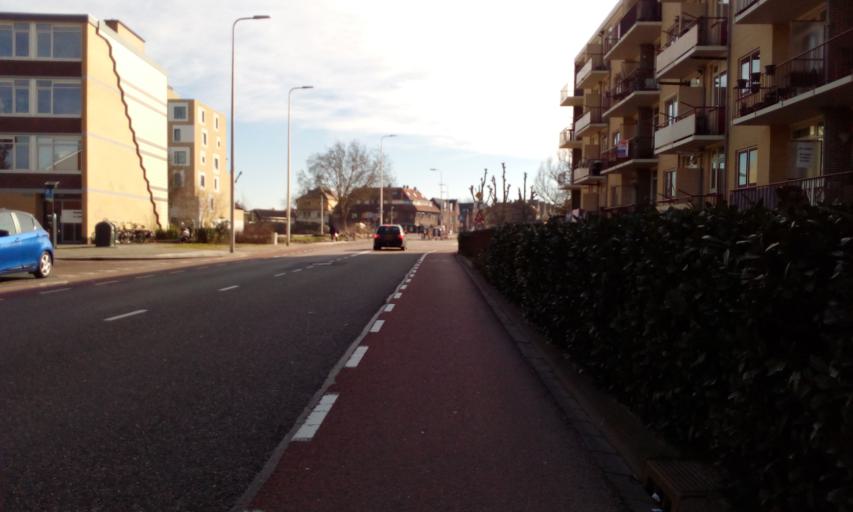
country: NL
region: South Holland
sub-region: Gemeente Alphen aan den Rijn
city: Alphen aan den Rijn
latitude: 52.1324
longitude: 4.6679
